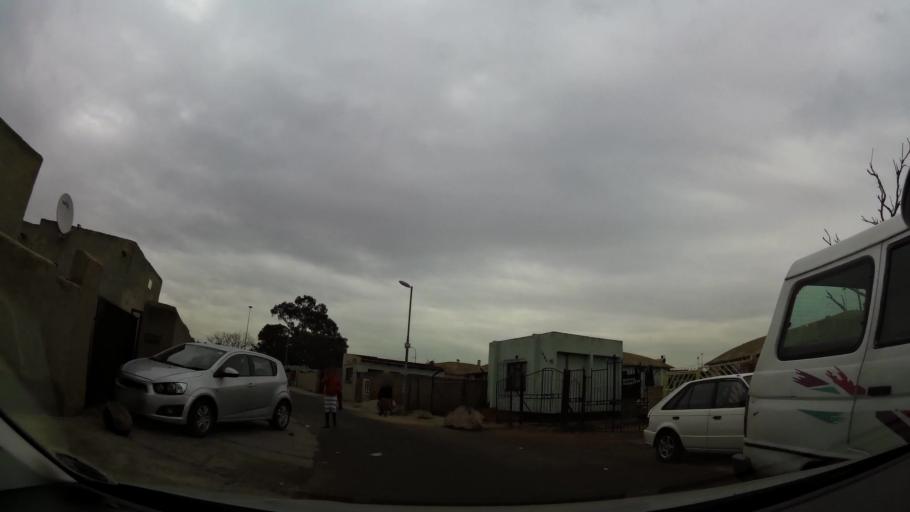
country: ZA
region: Gauteng
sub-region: City of Johannesburg Metropolitan Municipality
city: Soweto
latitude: -26.2543
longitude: 27.8761
